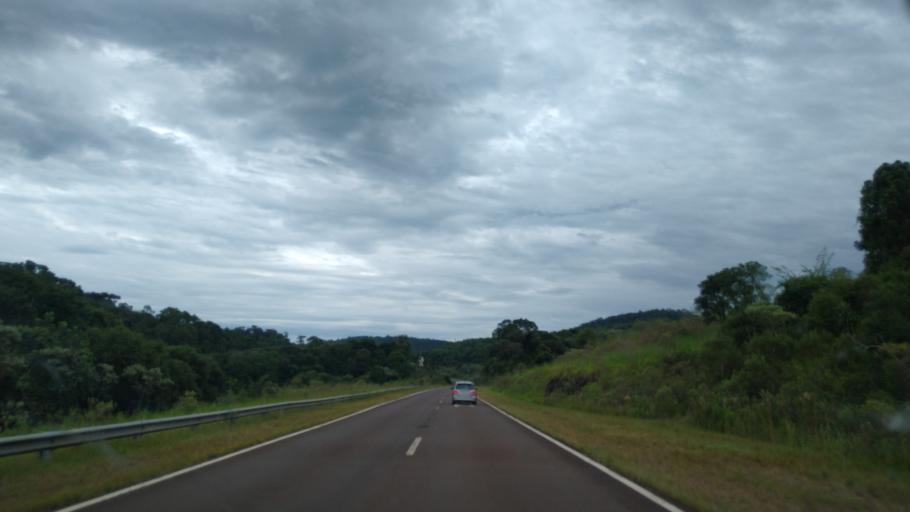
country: AR
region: Misiones
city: Bernardo de Irigoyen
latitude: -26.3341
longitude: -53.7660
